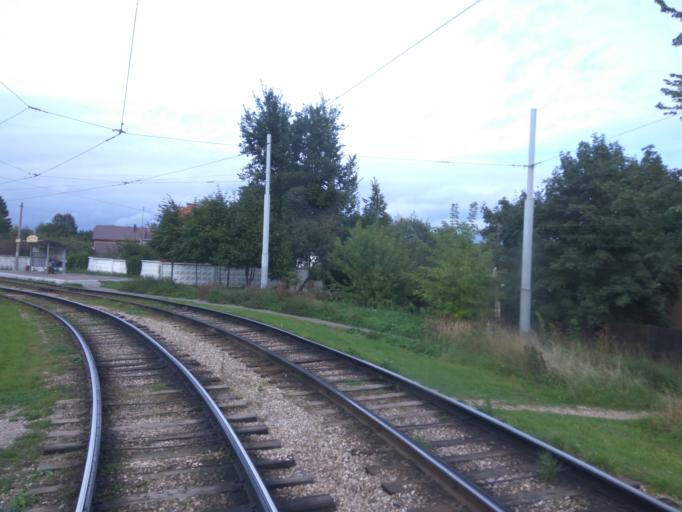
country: RU
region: Moskovskaya
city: Kolomna
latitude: 55.0605
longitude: 38.7578
